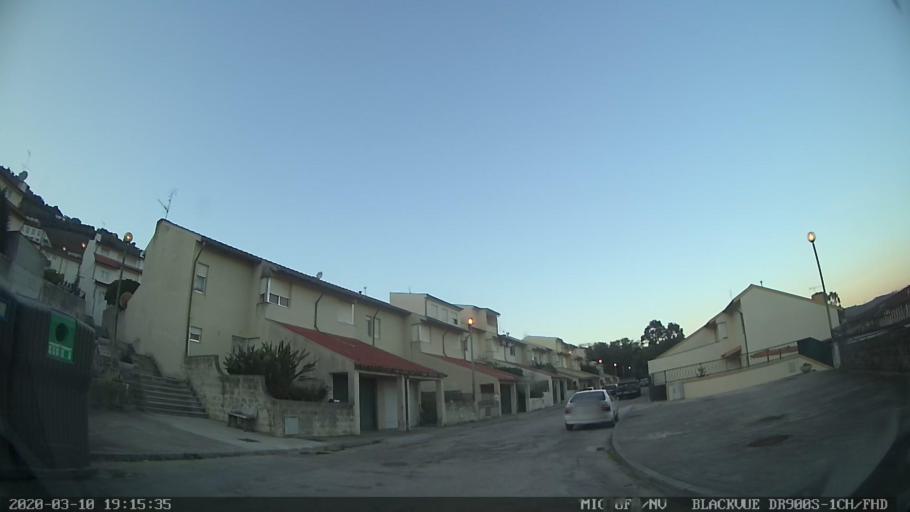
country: PT
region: Vila Real
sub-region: Peso da Regua
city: Godim
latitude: 41.1689
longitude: -7.8062
